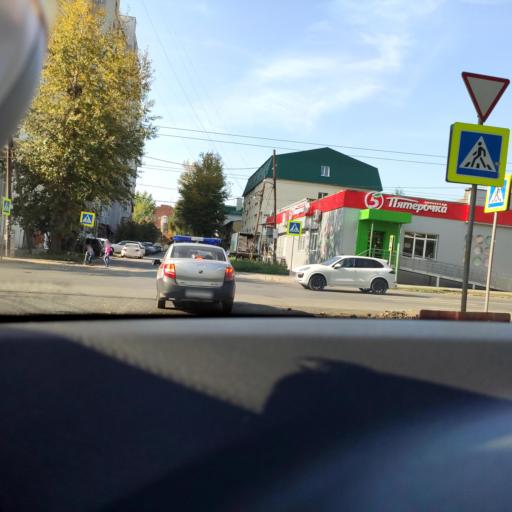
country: RU
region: Samara
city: Samara
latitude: 53.1848
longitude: 50.1077
